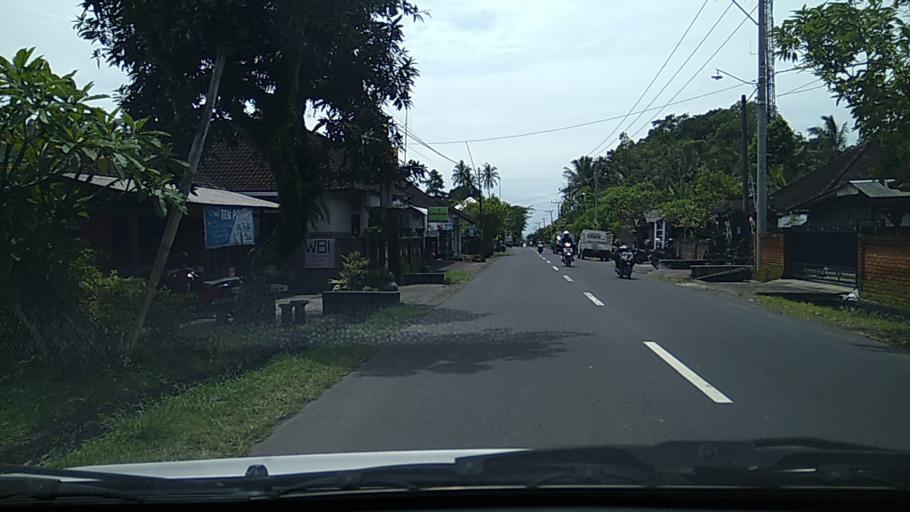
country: ID
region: Bali
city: Wanasari Baleran
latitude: -8.4785
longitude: 115.1361
